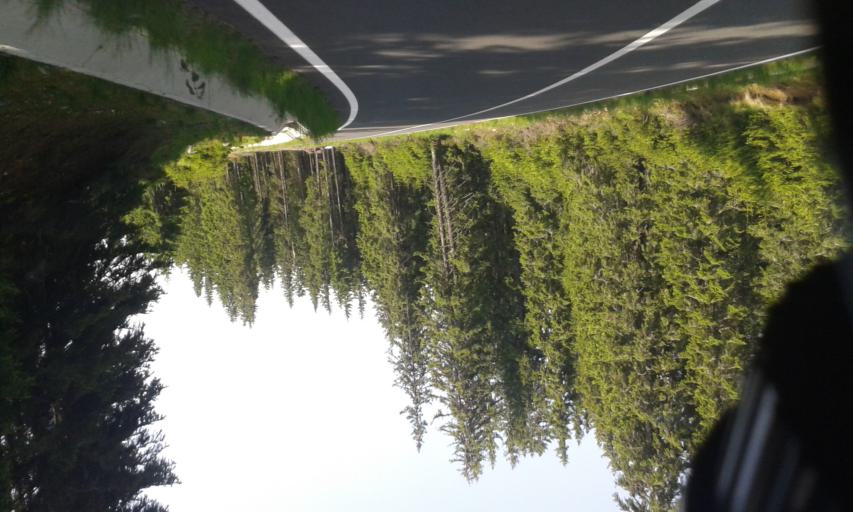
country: RO
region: Hunedoara
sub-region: Oras Petrila
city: Petrila
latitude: 45.4866
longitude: 23.6395
